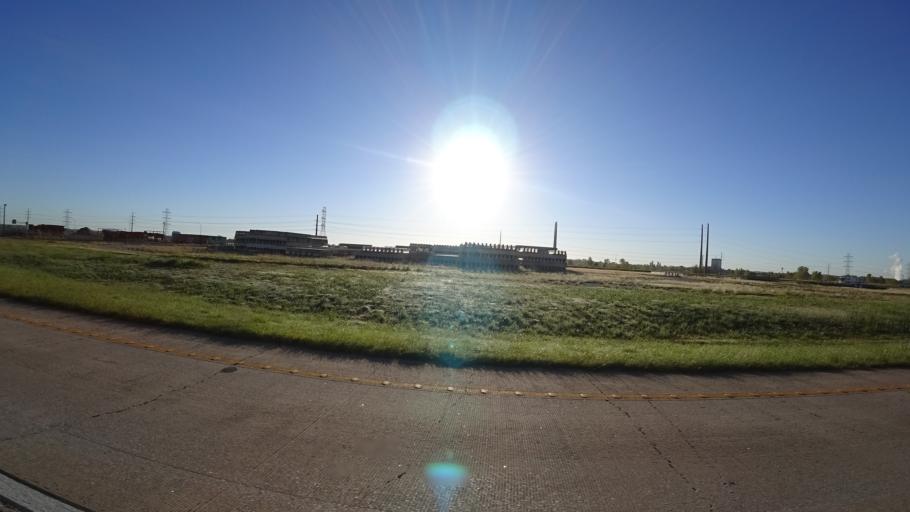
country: US
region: Texas
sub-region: Travis County
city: Hornsby Bend
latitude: 30.2366
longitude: -97.6173
